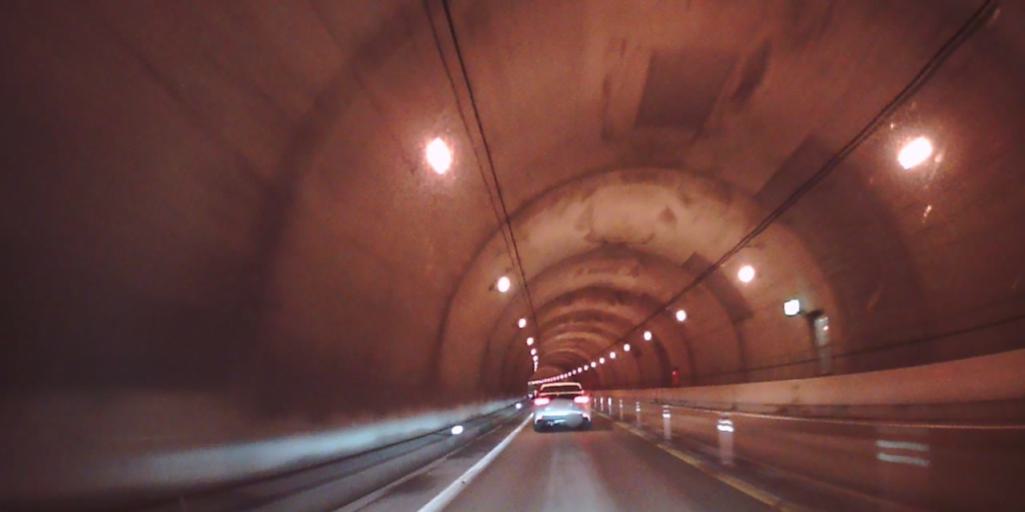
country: JP
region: Hokkaido
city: Date
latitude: 42.5541
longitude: 140.7850
